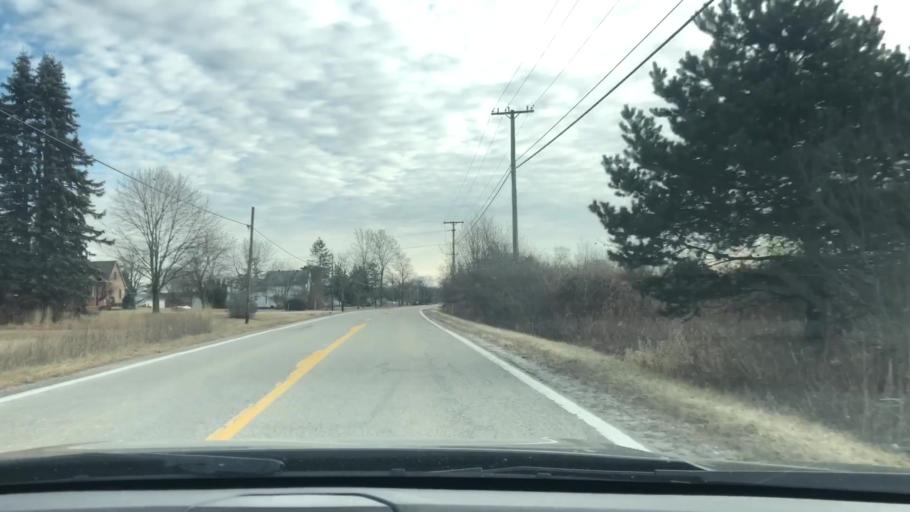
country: US
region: Michigan
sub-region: Macomb County
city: Shelby
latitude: 42.7302
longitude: -82.9883
